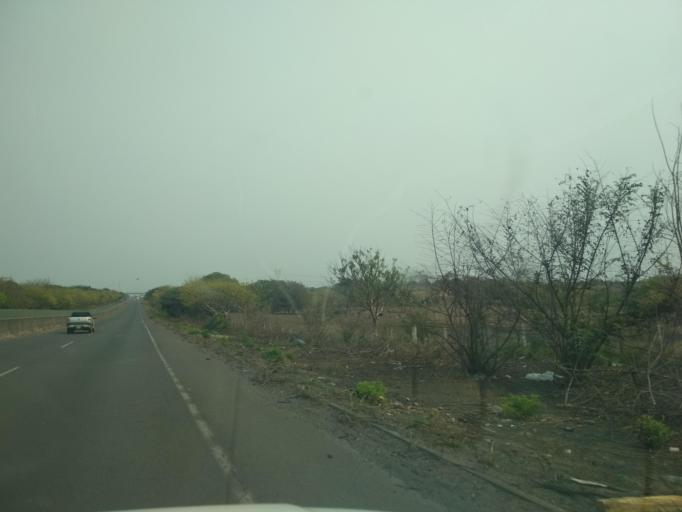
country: MX
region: Veracruz
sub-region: Veracruz
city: Las Amapolas
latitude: 19.1216
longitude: -96.2377
